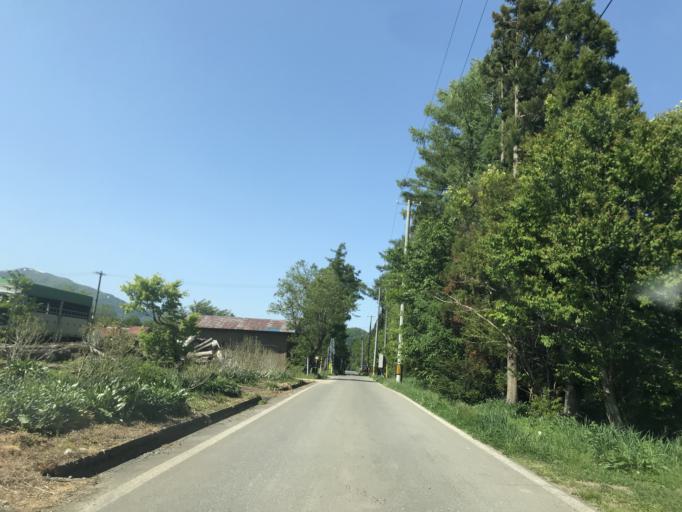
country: JP
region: Iwate
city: Shizukuishi
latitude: 39.5571
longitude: 140.8311
